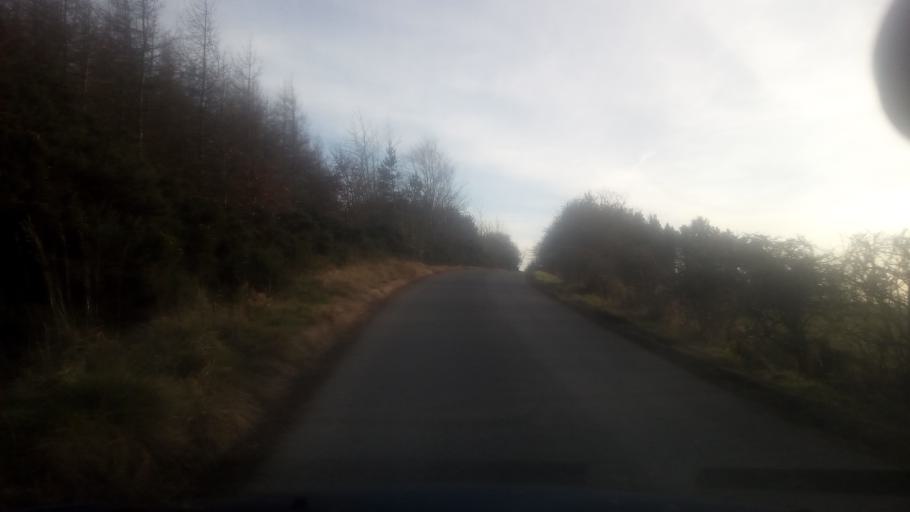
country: GB
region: Scotland
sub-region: The Scottish Borders
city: Jedburgh
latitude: 55.4074
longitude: -2.6002
